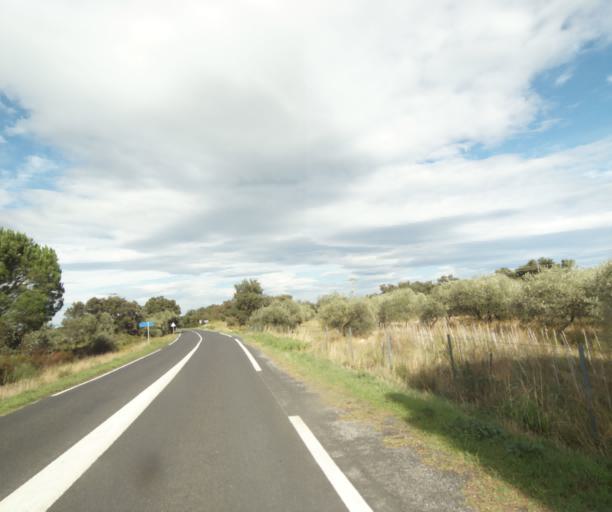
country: FR
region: Languedoc-Roussillon
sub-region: Departement des Pyrenees-Orientales
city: Sant Andreu de Sureda
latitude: 42.5358
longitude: 2.9948
